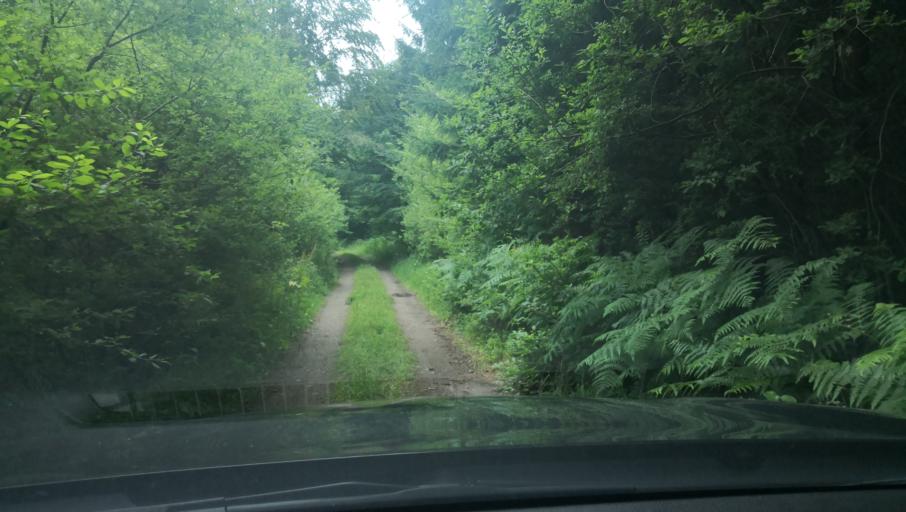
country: SE
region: Skane
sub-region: Simrishamns Kommun
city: Kivik
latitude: 55.6172
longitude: 14.1074
